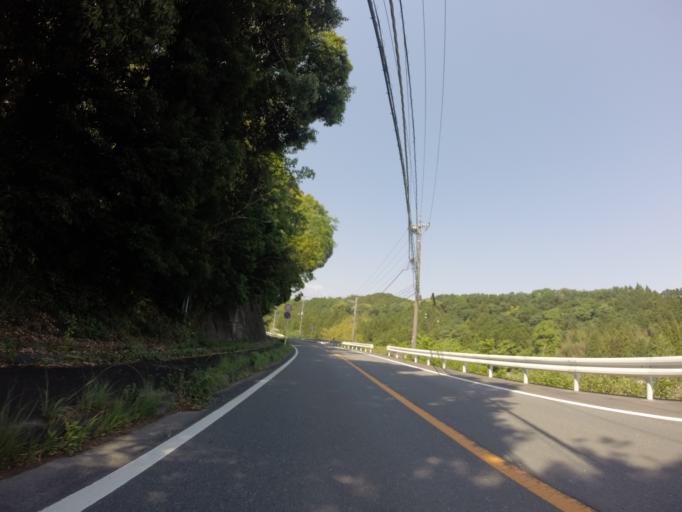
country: JP
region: Shizuoka
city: Fujinomiya
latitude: 35.2024
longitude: 138.5859
